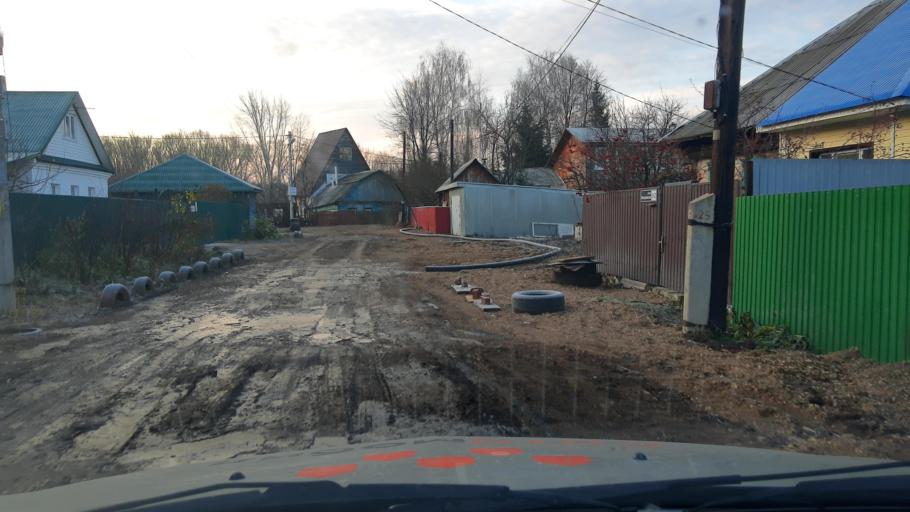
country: RU
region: Bashkortostan
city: Ufa
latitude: 54.7973
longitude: 56.1477
